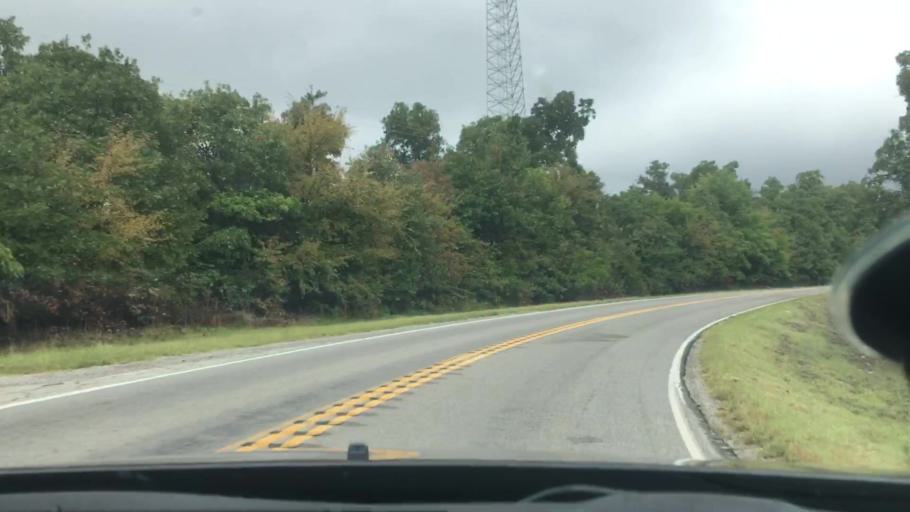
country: US
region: Oklahoma
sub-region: Sequoyah County
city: Vian
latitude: 35.6279
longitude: -94.9651
